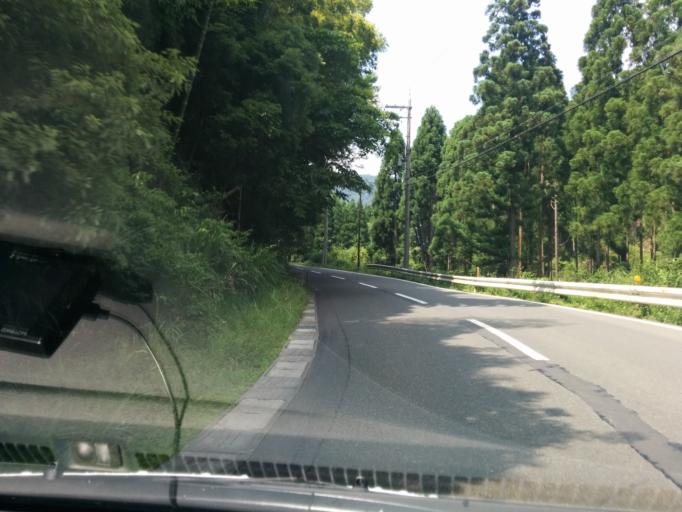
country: JP
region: Kyoto
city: Miyazu
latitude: 35.4351
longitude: 135.1596
